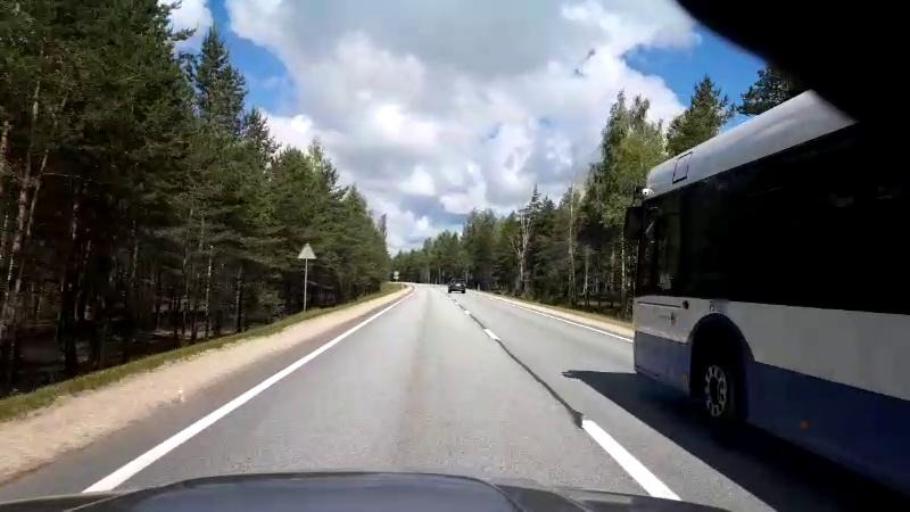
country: LV
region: Riga
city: Bergi
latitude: 56.9628
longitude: 24.3713
